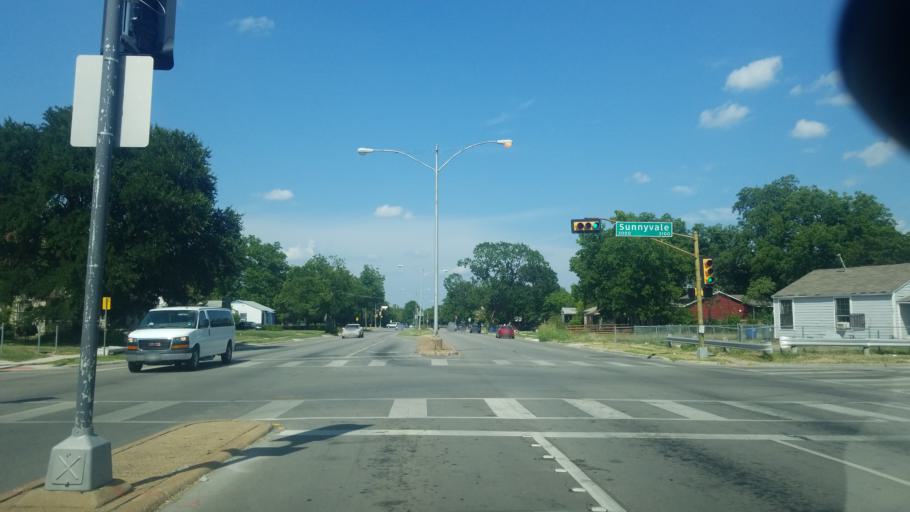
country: US
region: Texas
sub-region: Dallas County
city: Dallas
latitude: 32.7165
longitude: -96.7878
